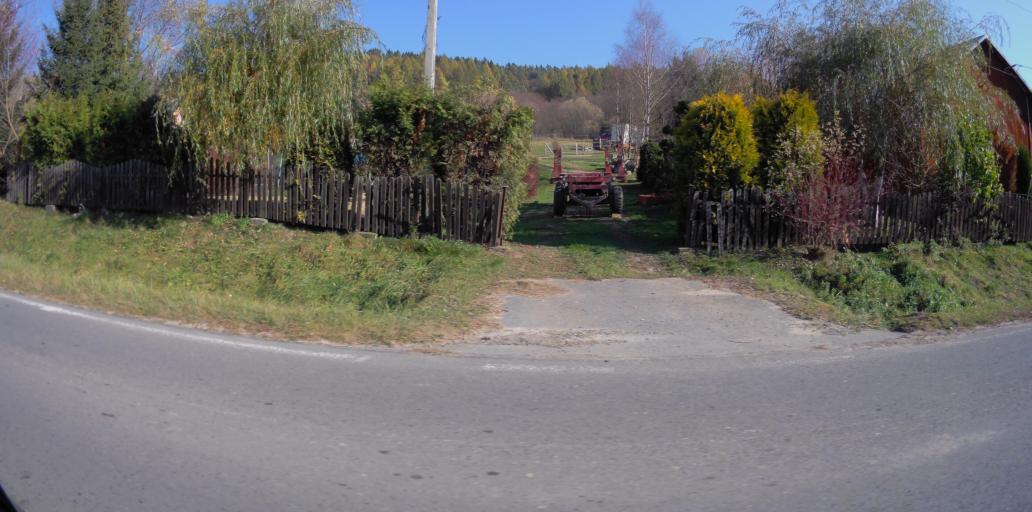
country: PL
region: Subcarpathian Voivodeship
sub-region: Powiat bieszczadzki
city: Ustrzyki Dolne
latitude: 49.4818
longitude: 22.6655
